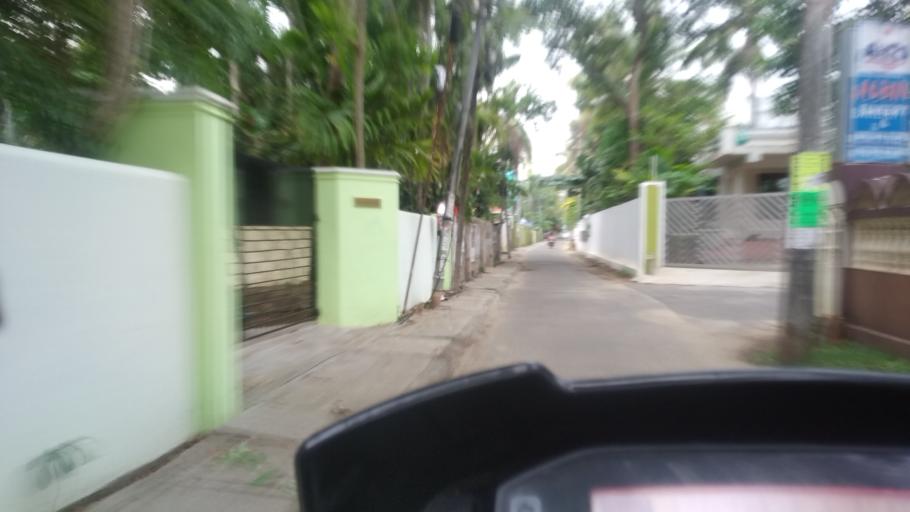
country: IN
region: Kerala
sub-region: Ernakulam
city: Elur
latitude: 10.0638
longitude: 76.2160
